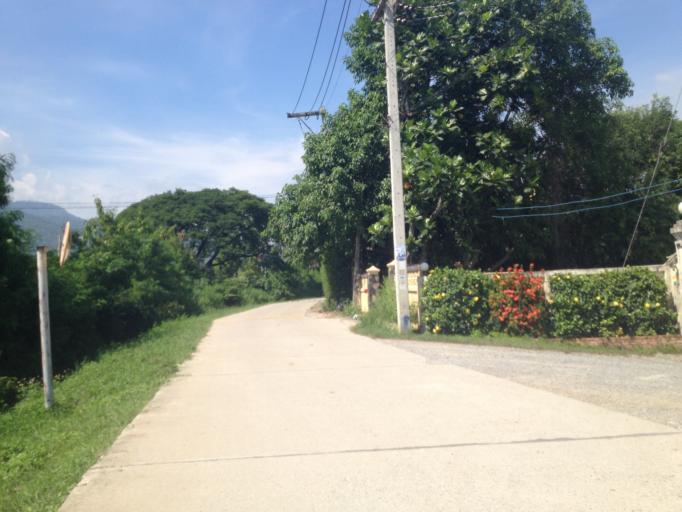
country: TH
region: Chiang Mai
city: Chiang Mai
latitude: 18.7584
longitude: 98.9440
